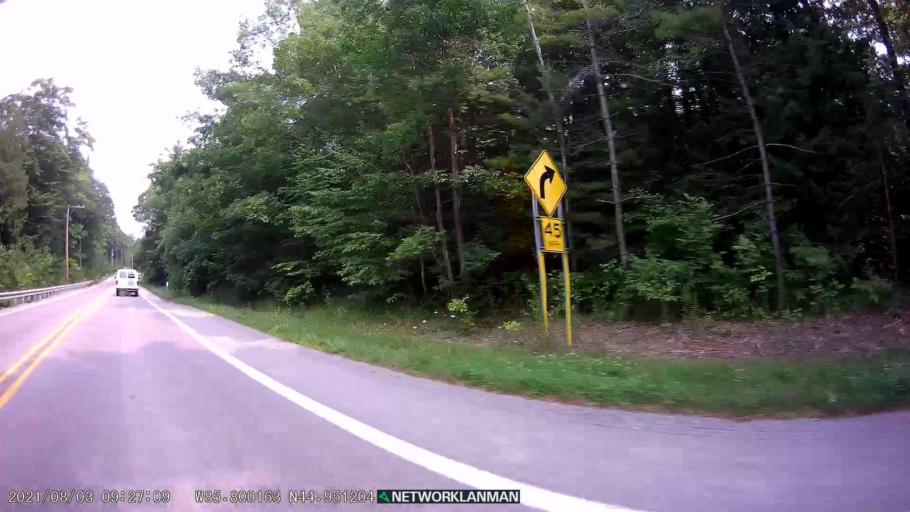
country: US
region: Michigan
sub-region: Leelanau County
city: Leland
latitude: 44.9514
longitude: -85.8002
